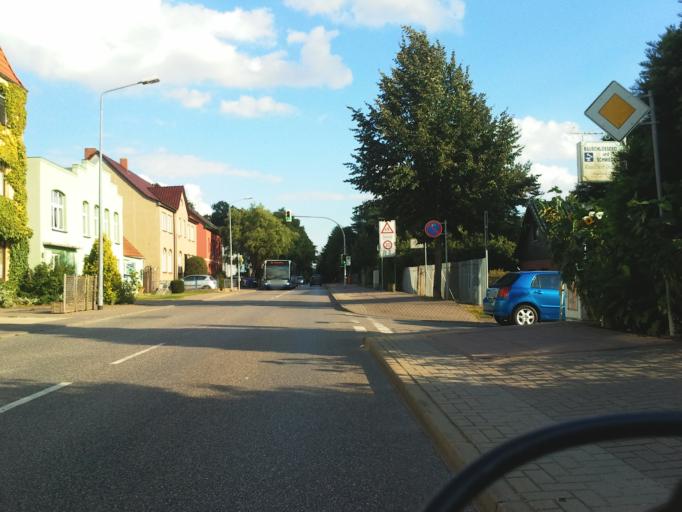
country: DE
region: Mecklenburg-Vorpommern
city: Rostock
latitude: 54.1013
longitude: 12.1193
